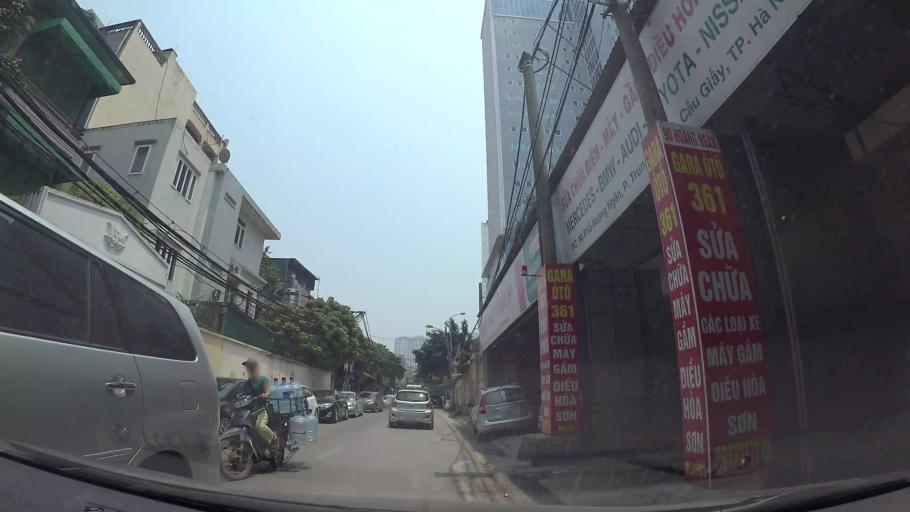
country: VN
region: Ha Noi
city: Thanh Xuan
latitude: 21.0086
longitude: 105.8078
